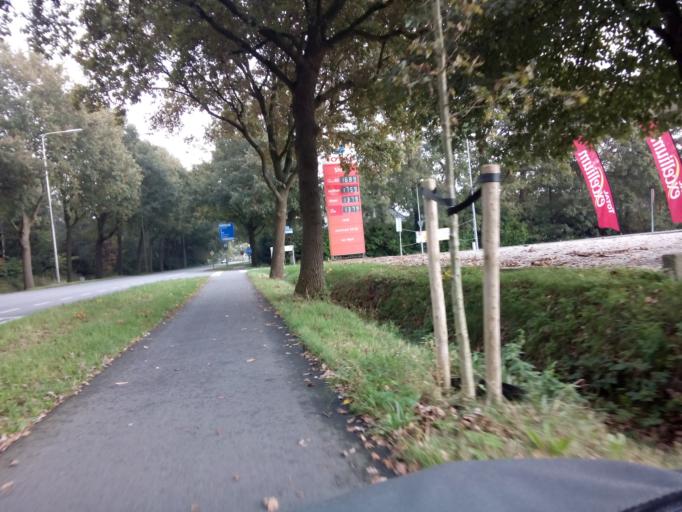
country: NL
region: Gelderland
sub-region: Gemeente Nunspeet
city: Nunspeet
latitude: 52.3714
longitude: 5.7540
